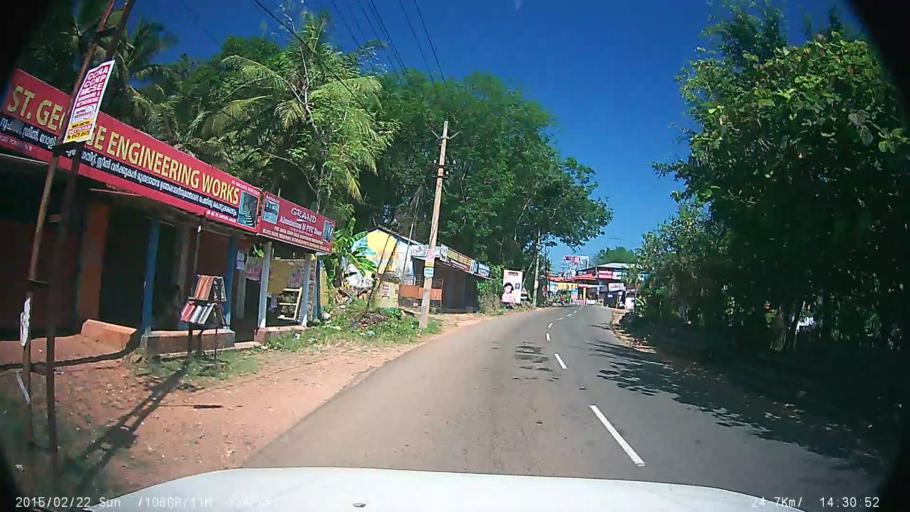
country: IN
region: Kerala
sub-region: Kottayam
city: Erattupetta
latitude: 9.5658
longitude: 76.7508
